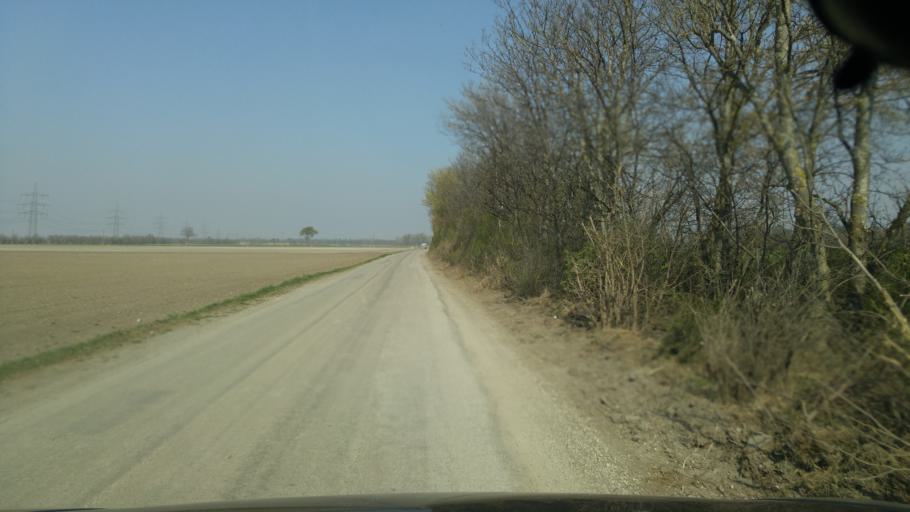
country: AT
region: Lower Austria
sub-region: Politischer Bezirk Modling
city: Munchendorf
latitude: 48.0318
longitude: 16.3958
